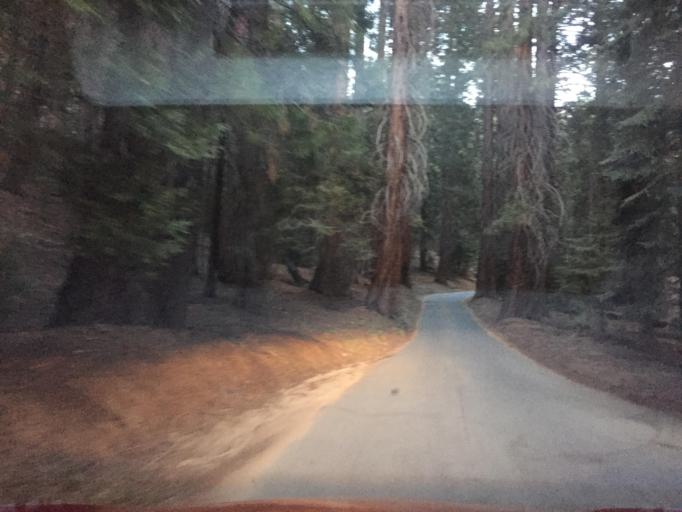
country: US
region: California
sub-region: Tulare County
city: Three Rivers
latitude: 36.4654
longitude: -118.6703
